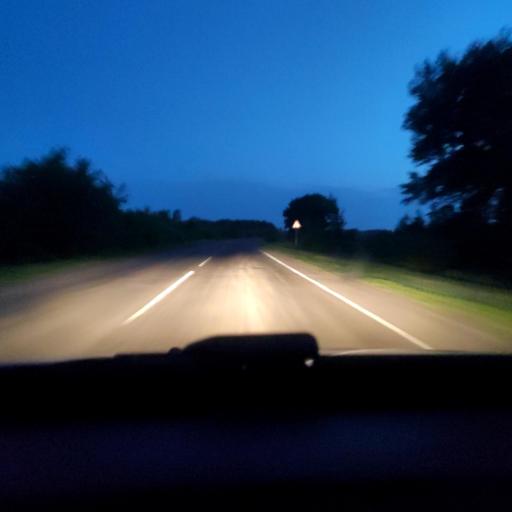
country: RU
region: Voronezj
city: Panino
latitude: 51.6394
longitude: 40.1093
